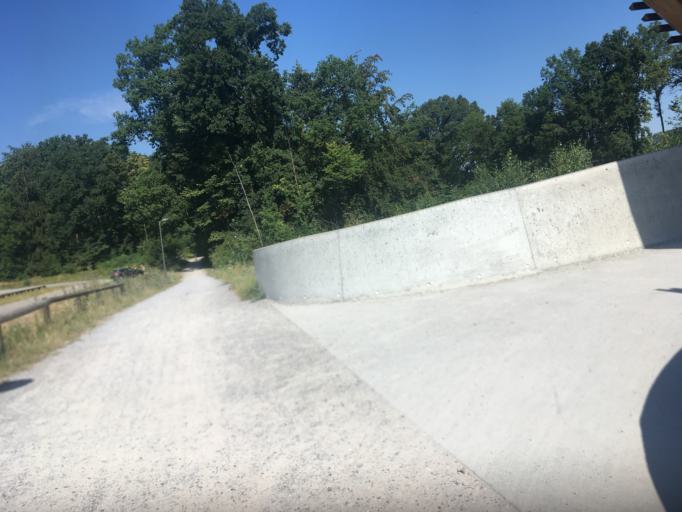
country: CH
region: Bern
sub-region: Emmental District
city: Lyssach
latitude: 47.0699
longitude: 7.6034
